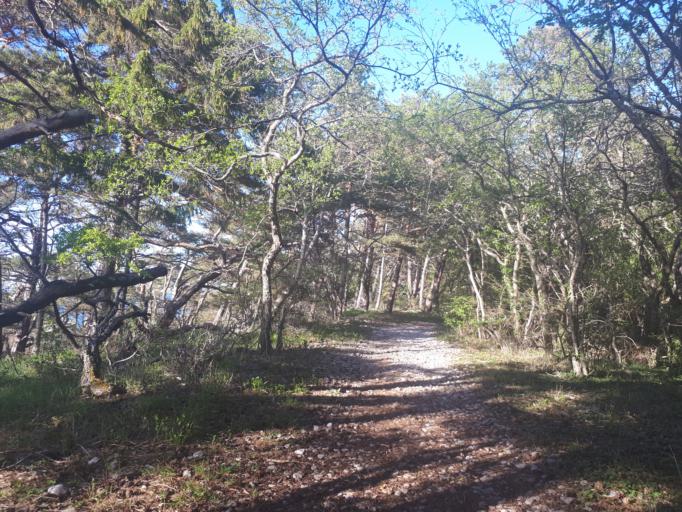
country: SE
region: Gotland
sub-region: Gotland
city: Vibble
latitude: 57.6129
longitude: 18.2482
